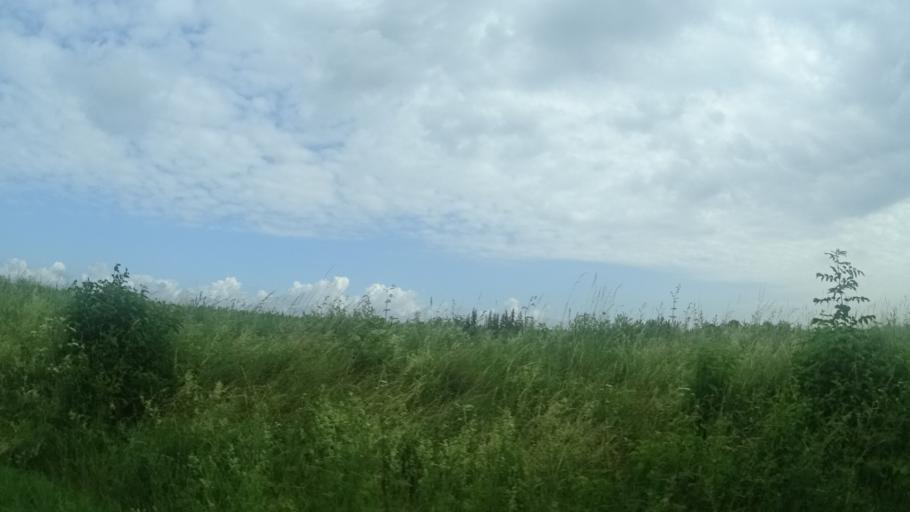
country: DE
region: Lower Saxony
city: Heyersum
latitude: 52.1859
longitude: 9.8207
